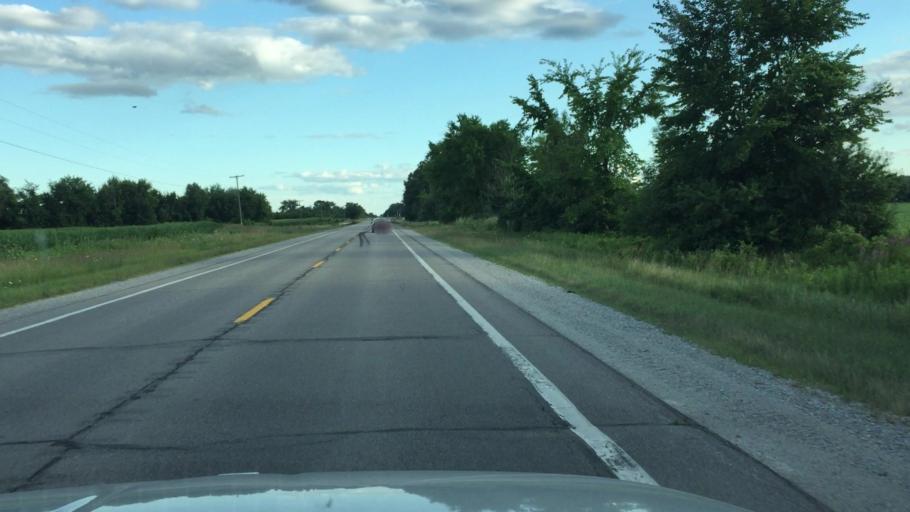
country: US
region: Michigan
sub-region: Saint Clair County
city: Yale
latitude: 43.0512
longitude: -82.7639
